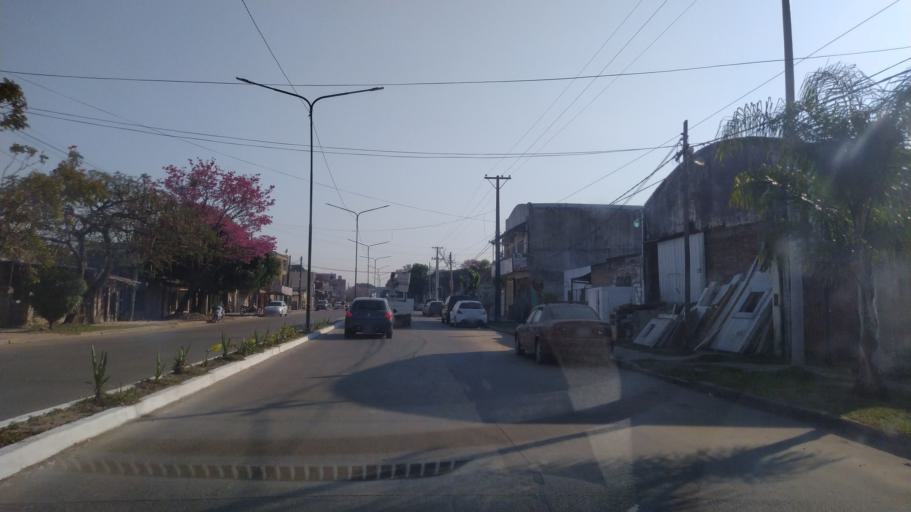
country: AR
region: Corrientes
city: Corrientes
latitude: -27.4919
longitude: -58.8172
